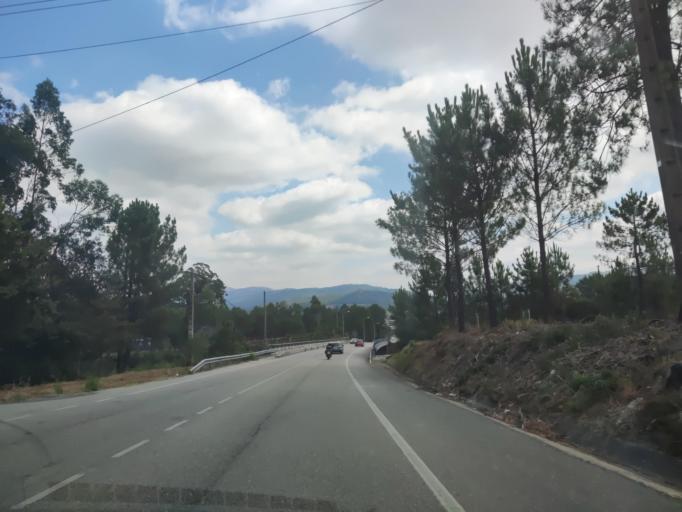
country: ES
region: Galicia
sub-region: Provincia de Pontevedra
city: Porrino
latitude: 42.1479
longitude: -8.6426
